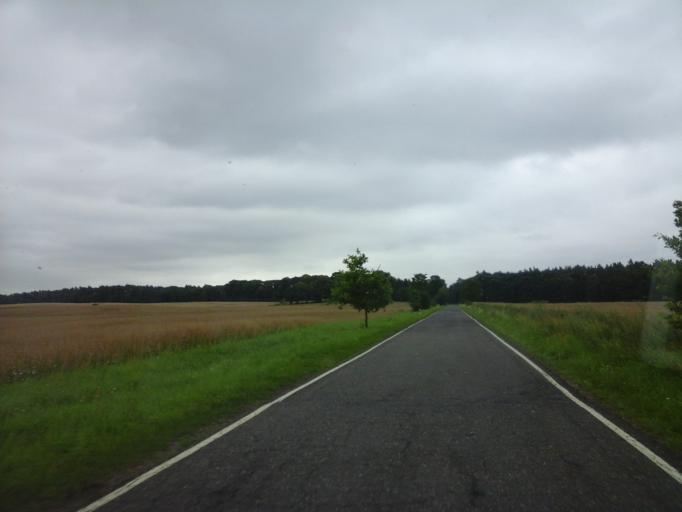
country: PL
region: West Pomeranian Voivodeship
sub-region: Powiat choszczenski
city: Pelczyce
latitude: 53.0987
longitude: 15.2646
